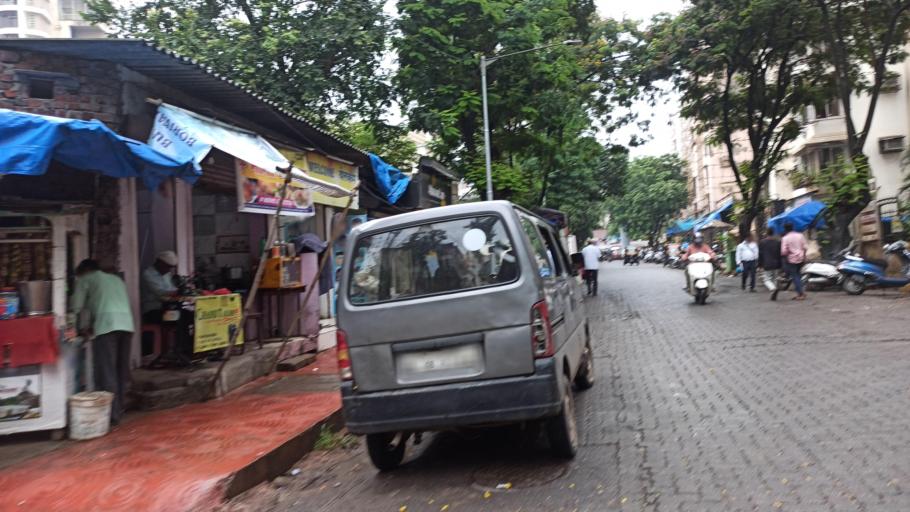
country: IN
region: Maharashtra
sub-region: Mumbai Suburban
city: Borivli
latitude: 19.2591
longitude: 72.8517
